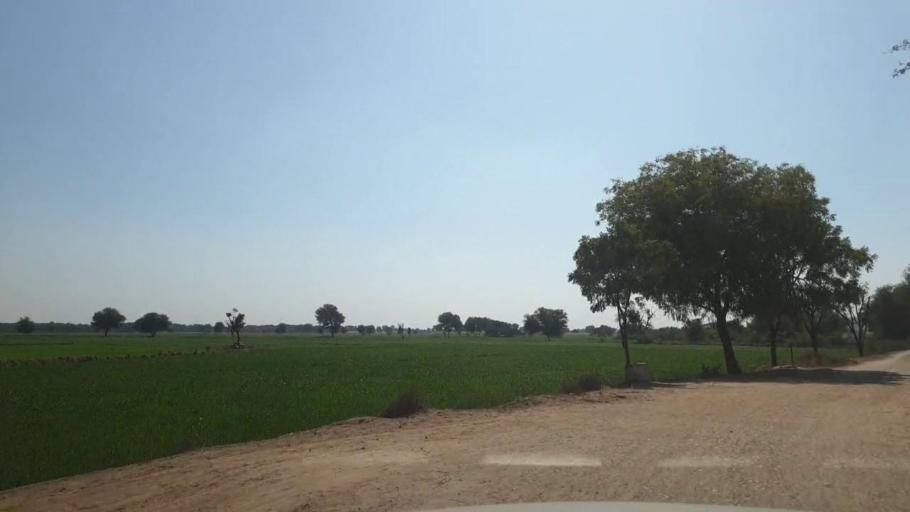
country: PK
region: Sindh
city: Tando Adam
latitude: 25.6382
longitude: 68.7072
